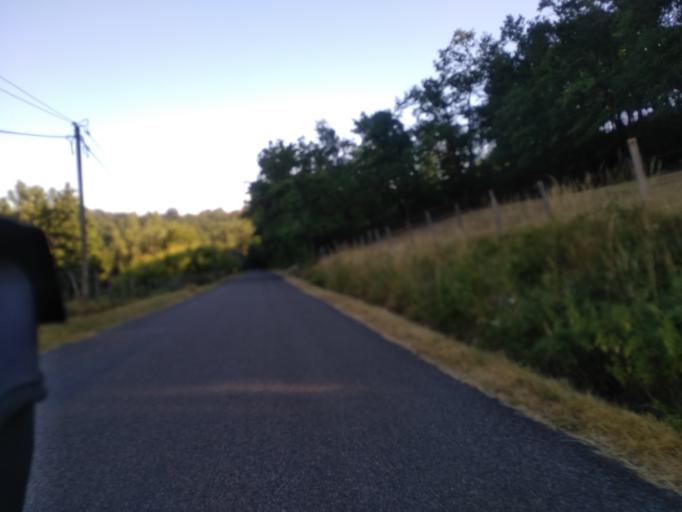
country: FR
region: Rhone-Alpes
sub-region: Departement de la Loire
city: Panissieres
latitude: 45.7489
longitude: 4.3144
